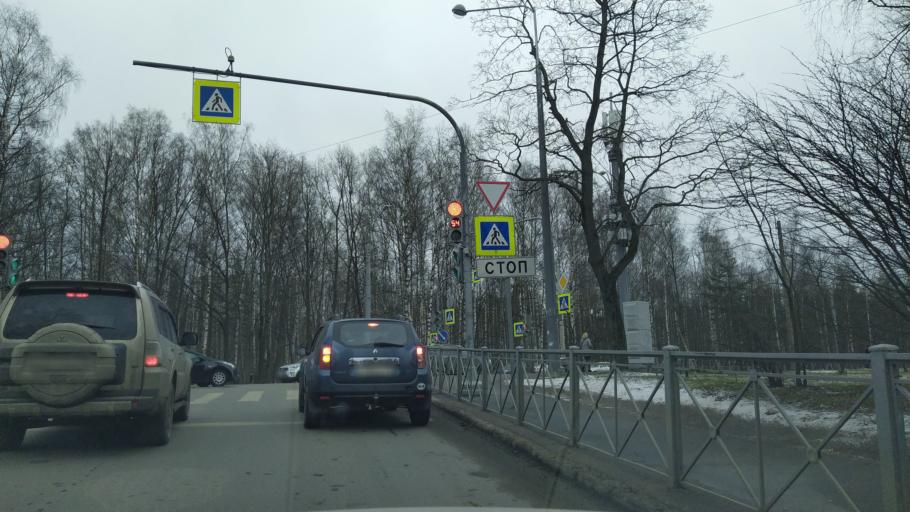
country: RU
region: Leningrad
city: Udel'naya
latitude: 60.0218
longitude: 30.3290
